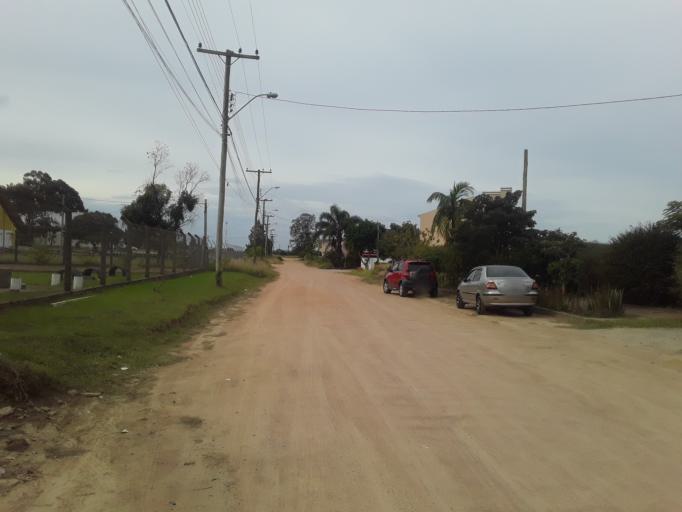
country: BR
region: Rio Grande do Sul
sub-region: Sao Lourenco Do Sul
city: Sao Lourenco do Sul
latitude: -31.3560
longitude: -51.9873
